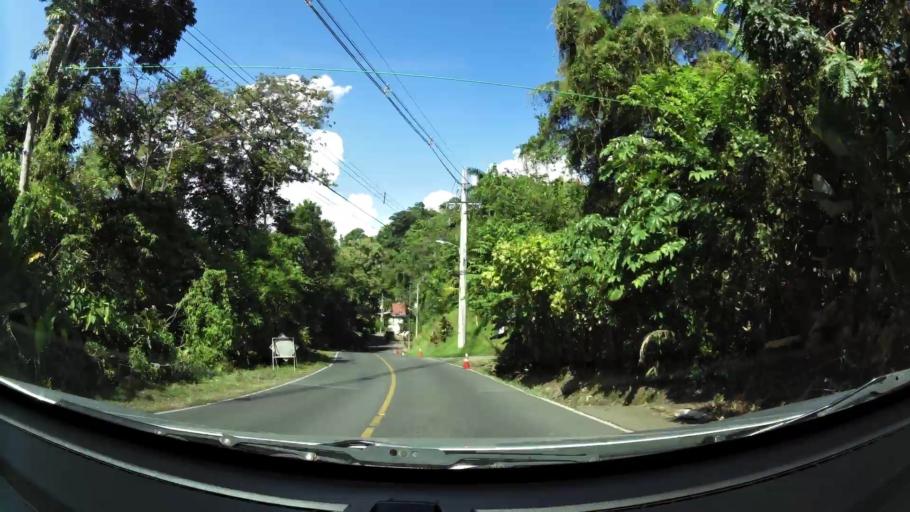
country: CR
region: Puntarenas
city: Quepos
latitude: 9.4216
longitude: -84.1588
